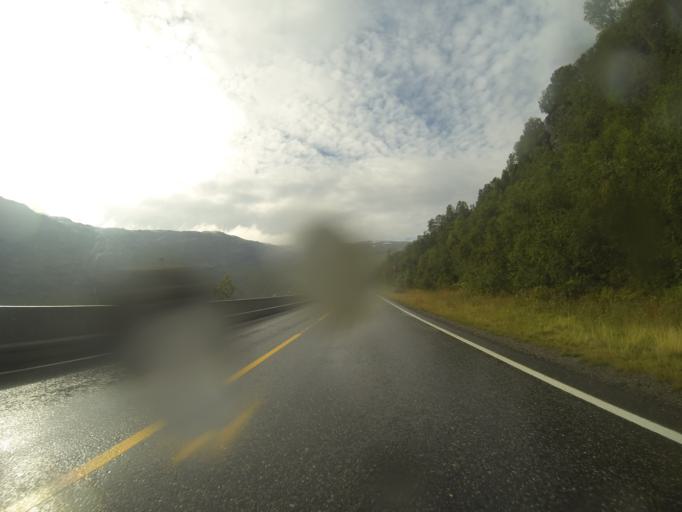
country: NO
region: Hordaland
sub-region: Odda
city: Odda
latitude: 59.8206
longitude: 6.7482
